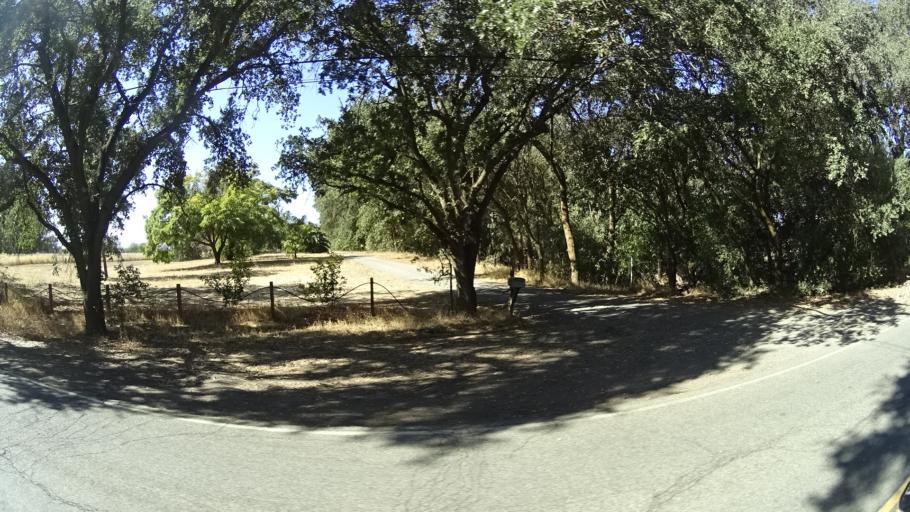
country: US
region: California
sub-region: Solano County
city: Dixon
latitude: 38.5469
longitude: -121.8562
